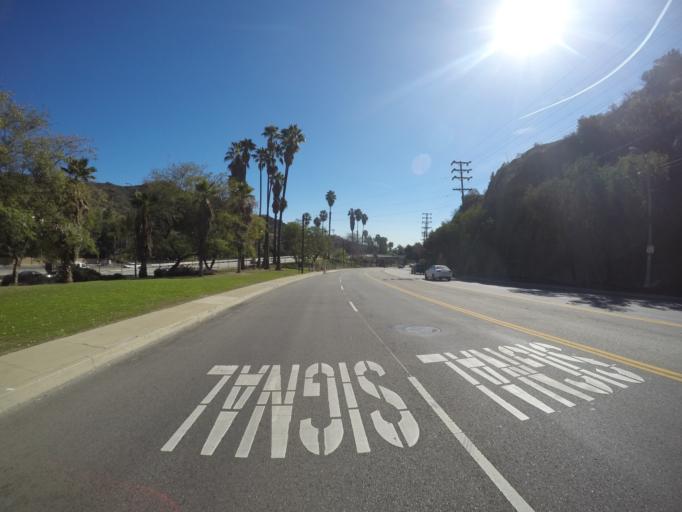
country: US
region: California
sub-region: Los Angeles County
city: Hollywood
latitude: 34.1189
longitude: -118.3387
